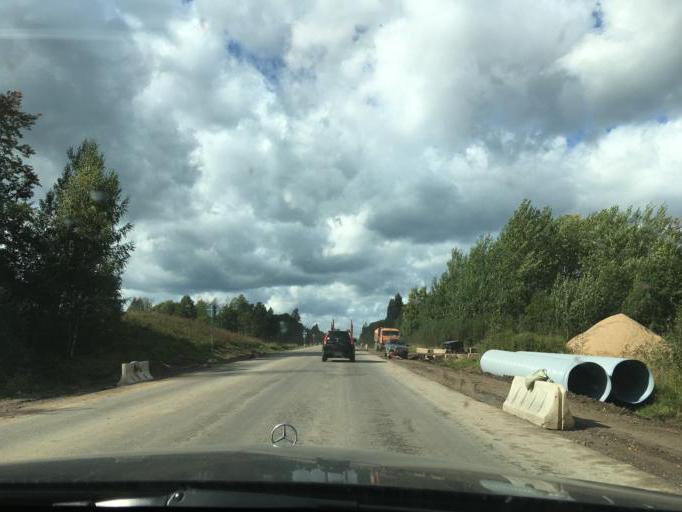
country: RU
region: Pskov
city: Novosokol'niki
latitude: 56.2823
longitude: 30.2873
